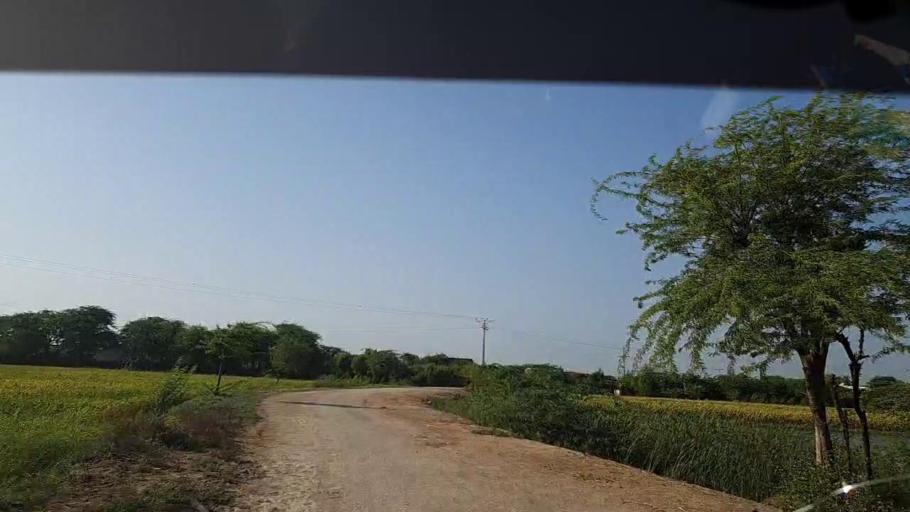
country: PK
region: Sindh
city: Badin
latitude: 24.6887
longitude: 68.8408
